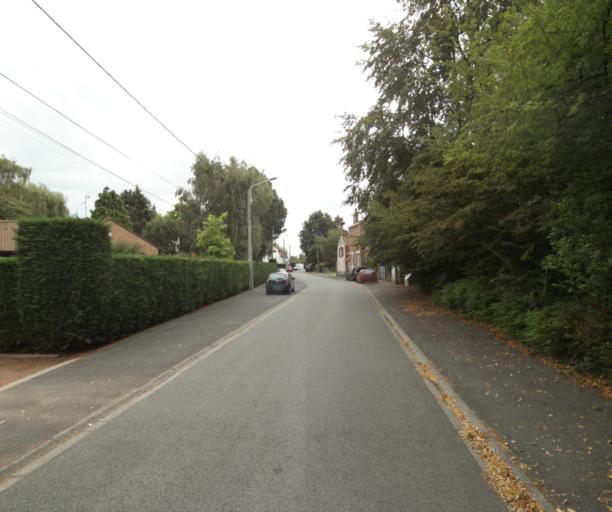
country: FR
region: Nord-Pas-de-Calais
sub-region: Departement du Nord
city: Villeneuve-d'Ascq
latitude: 50.6262
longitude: 3.1690
